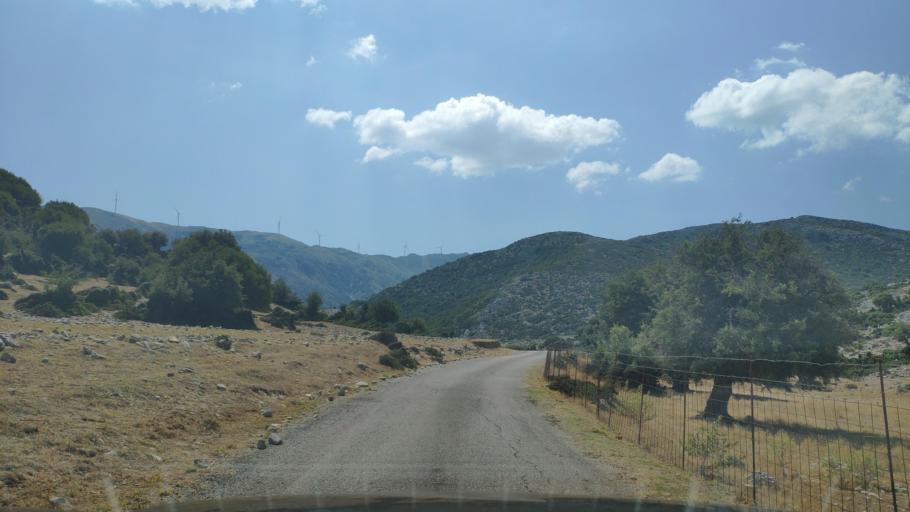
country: GR
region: West Greece
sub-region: Nomos Aitolias kai Akarnanias
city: Monastirakion
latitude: 38.7998
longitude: 20.9489
